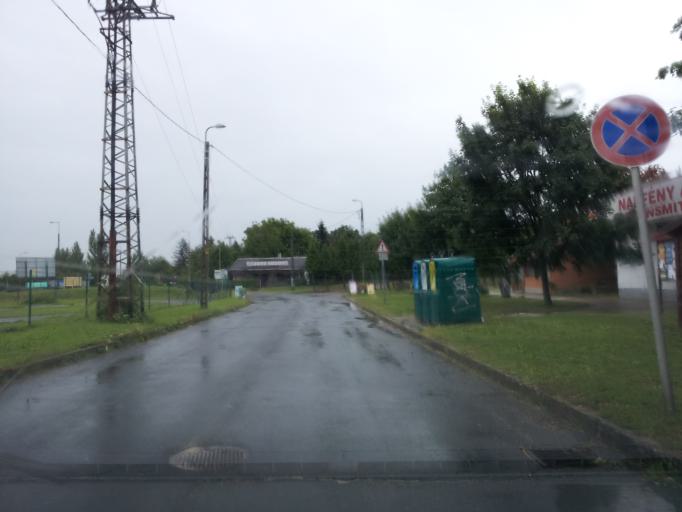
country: HU
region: Veszprem
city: Balatonkenese
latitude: 47.0157
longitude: 18.1666
